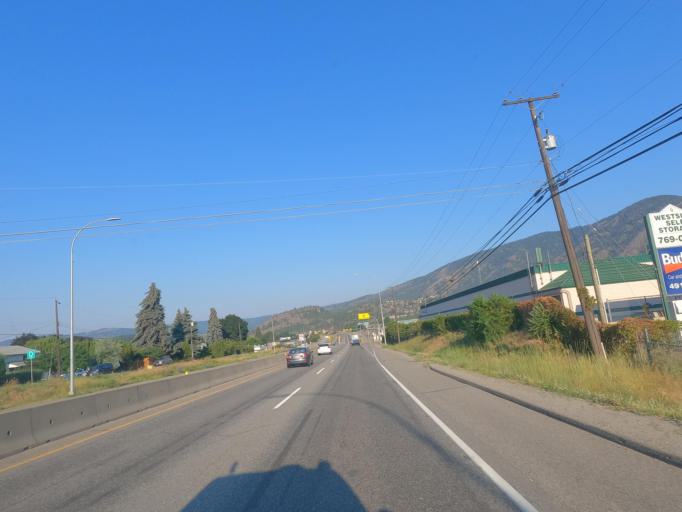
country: CA
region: British Columbia
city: West Kelowna
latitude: 49.8628
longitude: -119.5732
